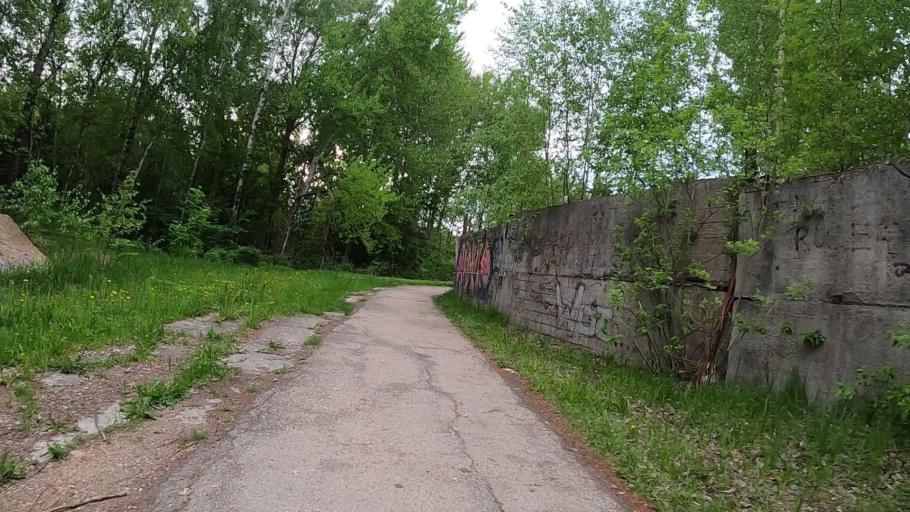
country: LV
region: Olaine
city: Olaine
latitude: 56.7929
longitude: 23.9272
